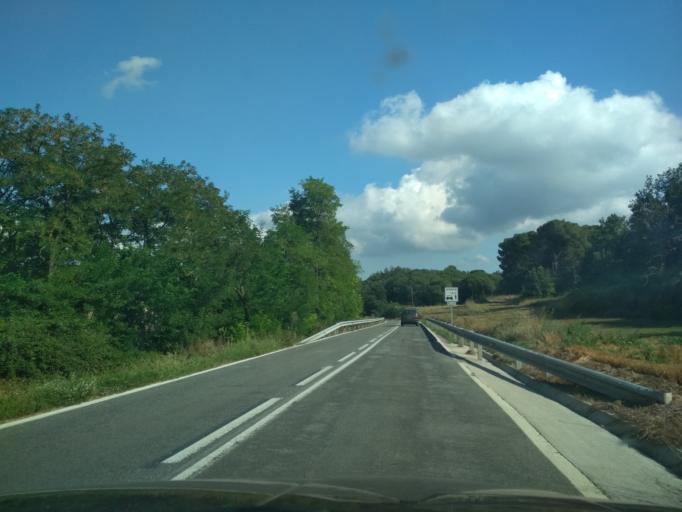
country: ES
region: Catalonia
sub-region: Provincia de Barcelona
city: Castelltercol
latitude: 41.7471
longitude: 2.1265
